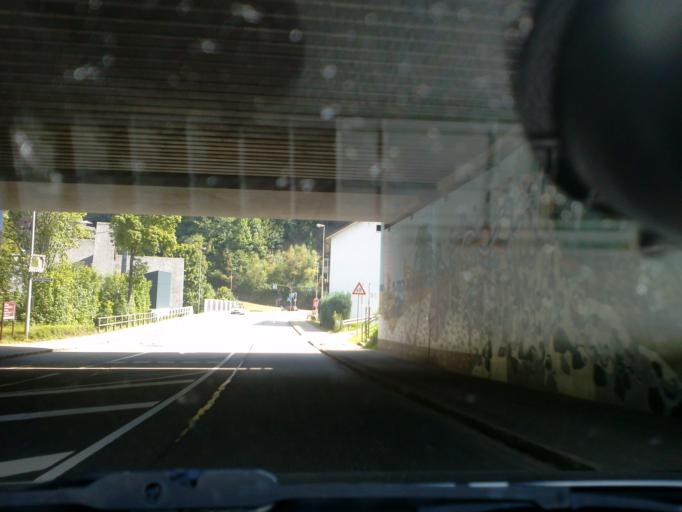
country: DE
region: Baden-Wuerttemberg
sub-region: Freiburg Region
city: Triberg im Schwarzwald
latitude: 48.1375
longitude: 8.2385
